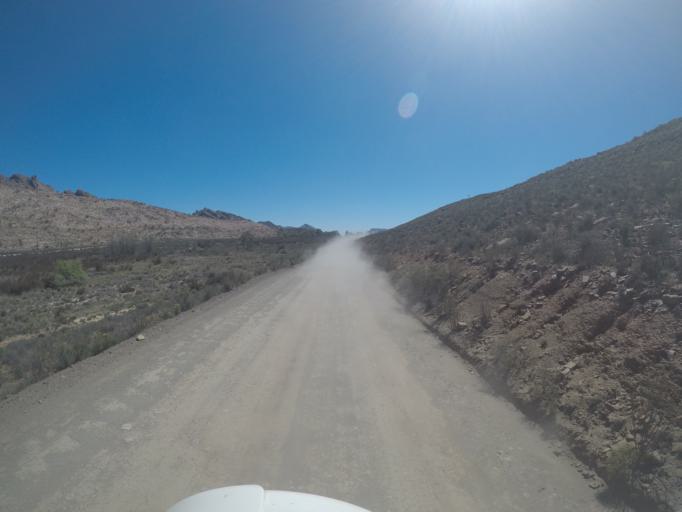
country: ZA
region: Western Cape
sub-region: Cape Winelands District Municipality
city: Ceres
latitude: -32.8203
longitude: 19.4527
